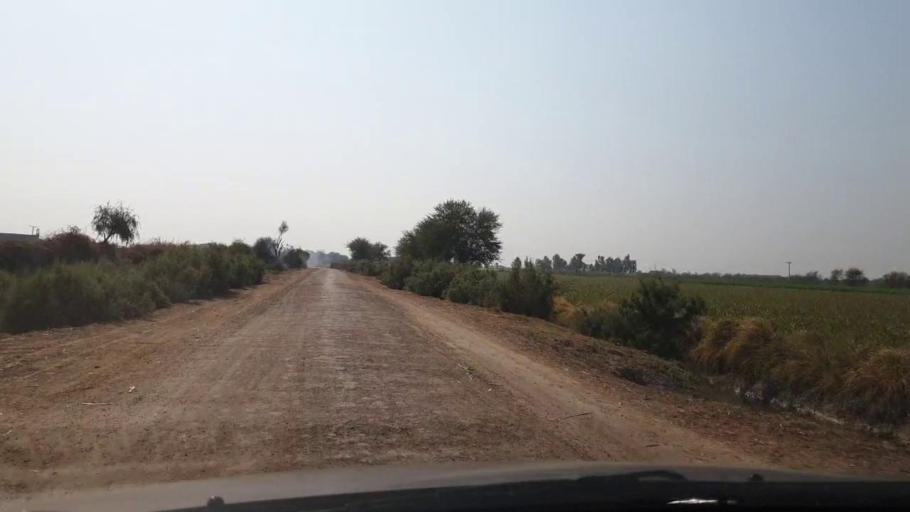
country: PK
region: Sindh
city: Jhol
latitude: 25.8441
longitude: 68.9884
